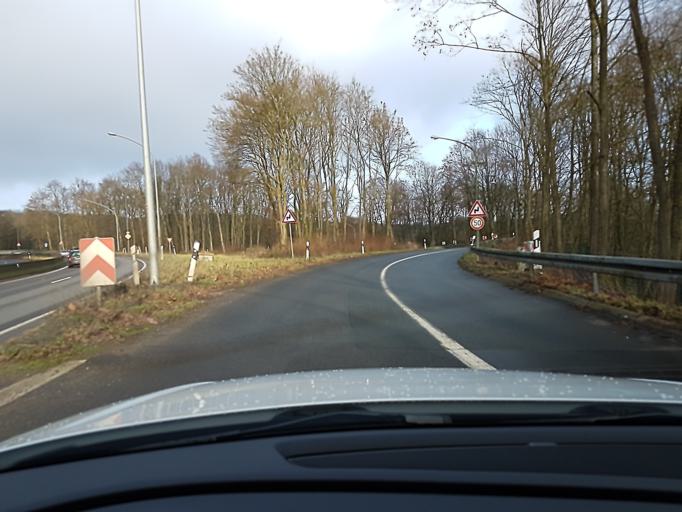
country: DE
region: North Rhine-Westphalia
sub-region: Regierungsbezirk Dusseldorf
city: Essen
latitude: 51.3933
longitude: 6.9970
